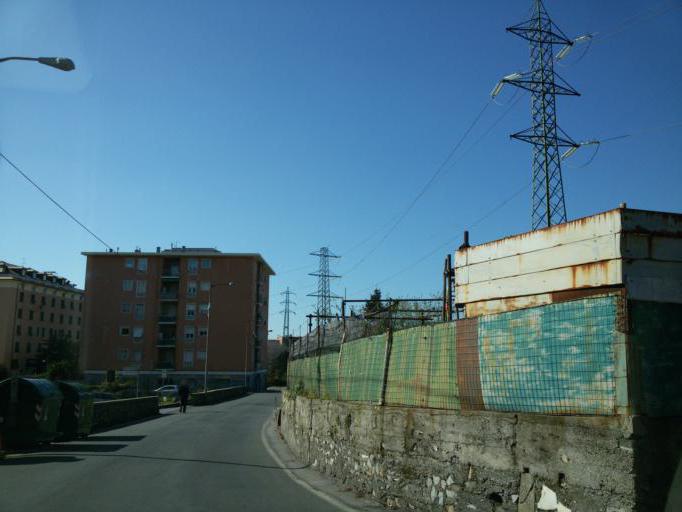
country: IT
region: Liguria
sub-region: Provincia di Genova
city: San Teodoro
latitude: 44.4160
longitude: 8.9047
